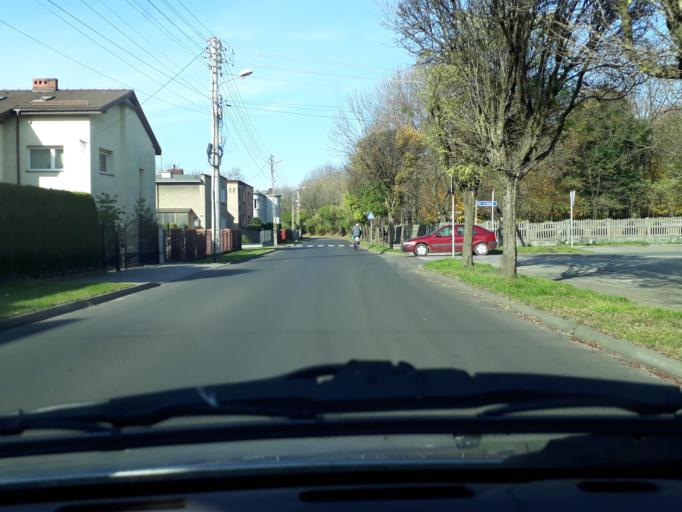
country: PL
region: Silesian Voivodeship
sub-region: Powiat tarnogorski
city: Tarnowskie Gory
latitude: 50.4353
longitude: 18.8660
